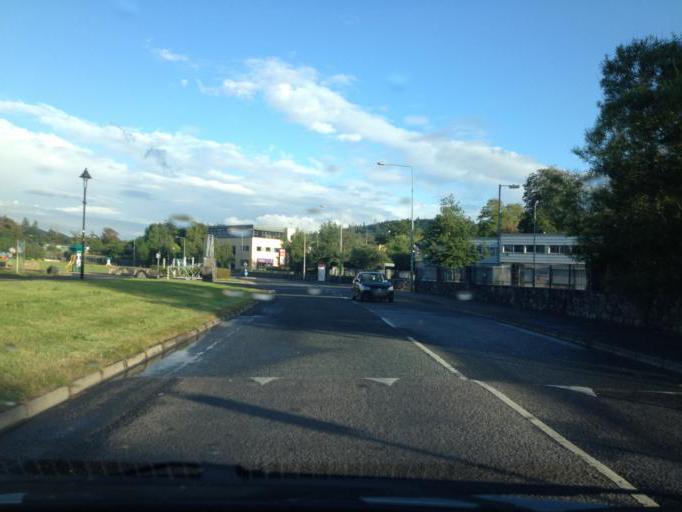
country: IE
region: Connaught
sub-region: Sligo
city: Sligo
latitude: 54.2674
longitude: -8.4552
